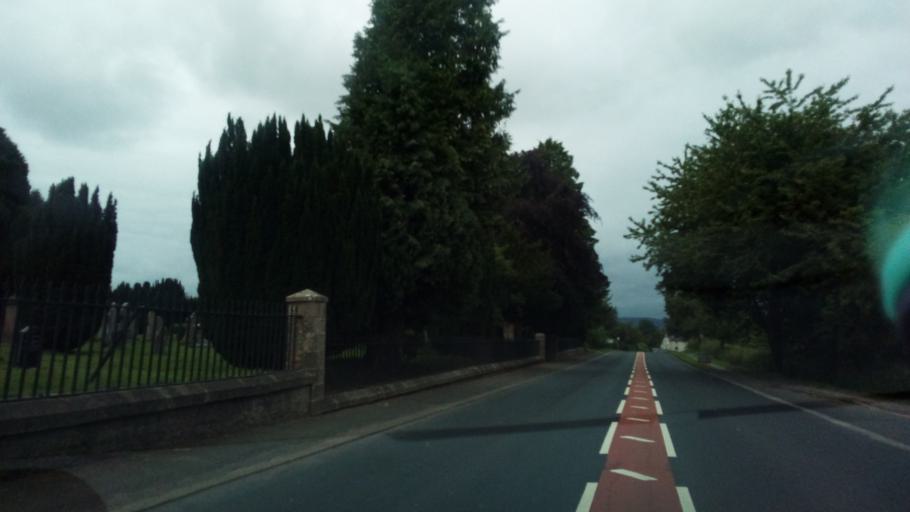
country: GB
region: England
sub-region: Cumbria
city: Kirkby Stephen
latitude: 54.4781
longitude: -2.3502
